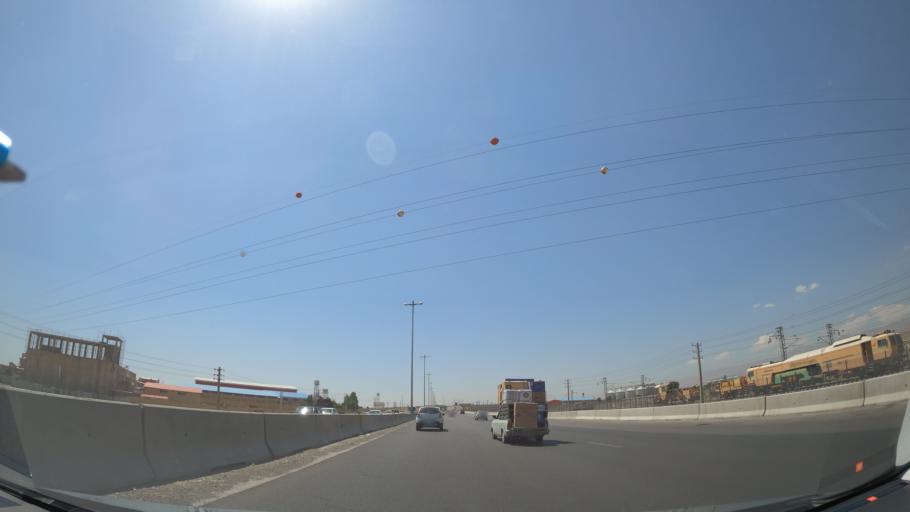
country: IR
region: Alborz
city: Karaj
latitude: 35.9067
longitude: 50.8428
